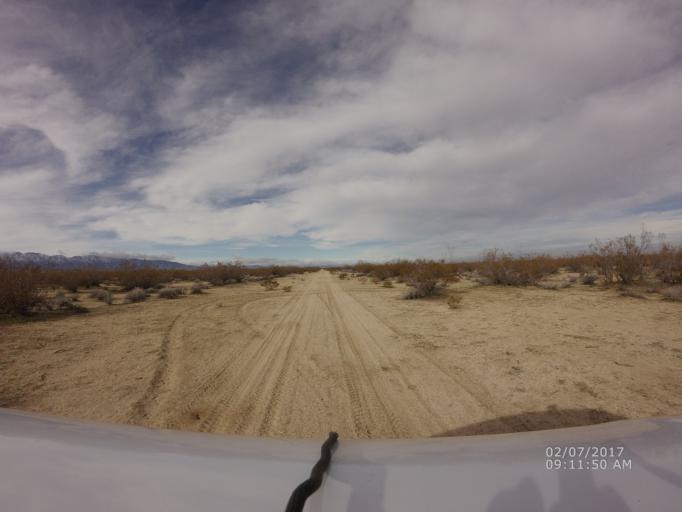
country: US
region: California
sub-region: Los Angeles County
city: Lake Los Angeles
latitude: 34.5276
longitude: -117.7332
